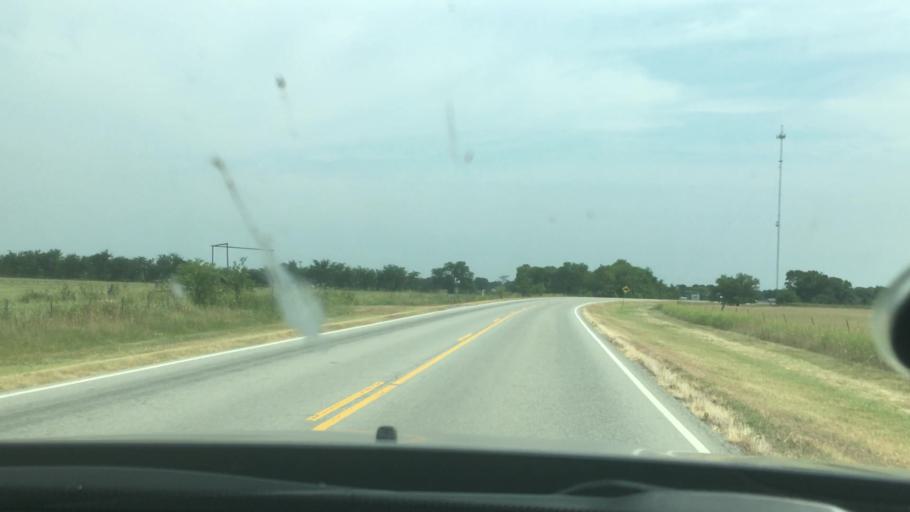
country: US
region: Oklahoma
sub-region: Coal County
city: Coalgate
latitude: 34.4844
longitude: -96.4245
